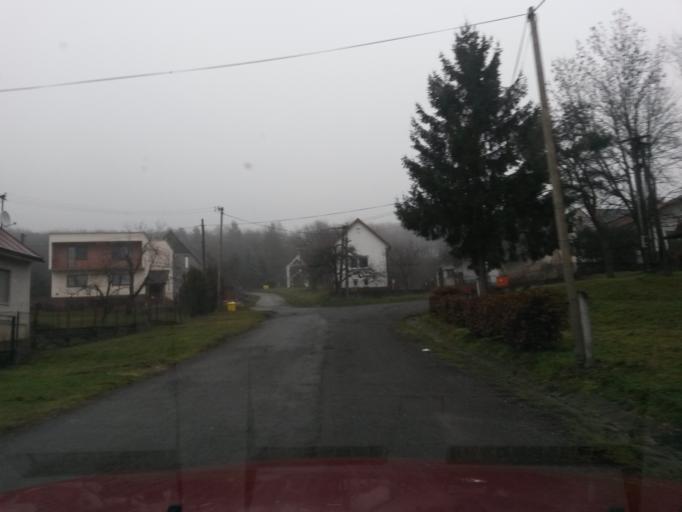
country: SK
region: Presovsky
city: Vranov nad Topl'ou
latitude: 48.8867
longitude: 21.7519
